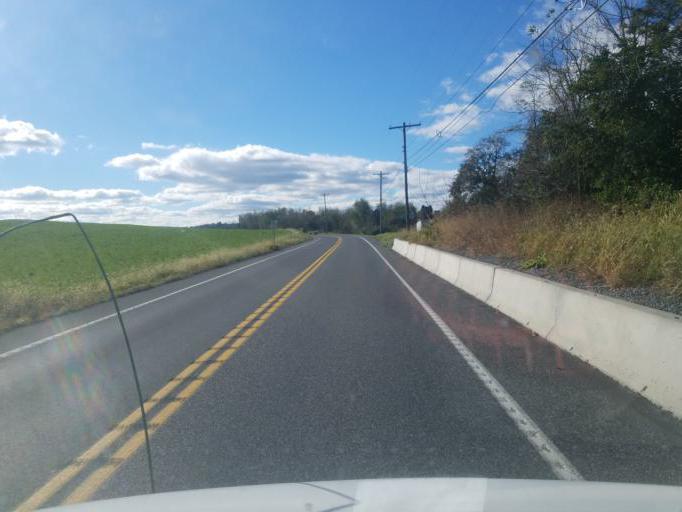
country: US
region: Pennsylvania
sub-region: Franklin County
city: Waynesboro
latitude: 39.7790
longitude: -77.5698
